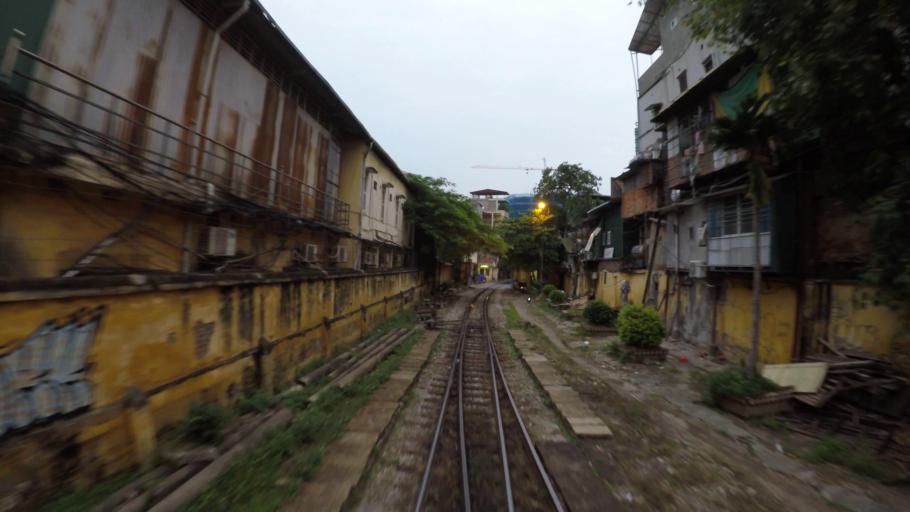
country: VN
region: Ha Noi
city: Hoan Kiem
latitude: 21.0322
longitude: 105.8454
